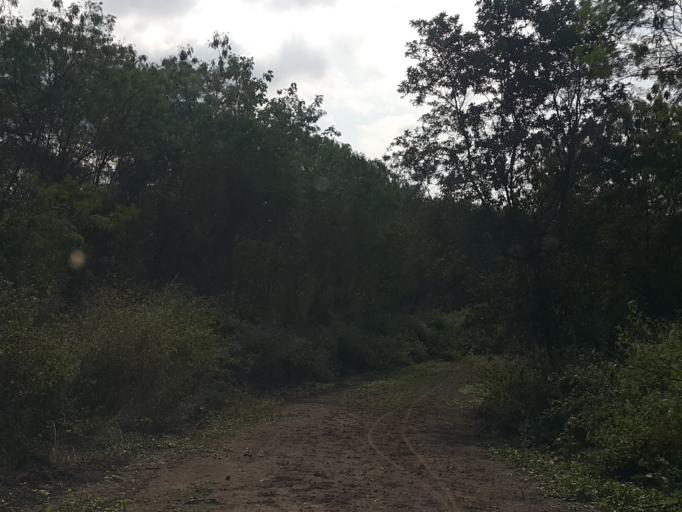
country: TH
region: Lampang
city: Mae Mo
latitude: 18.3403
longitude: 99.7668
